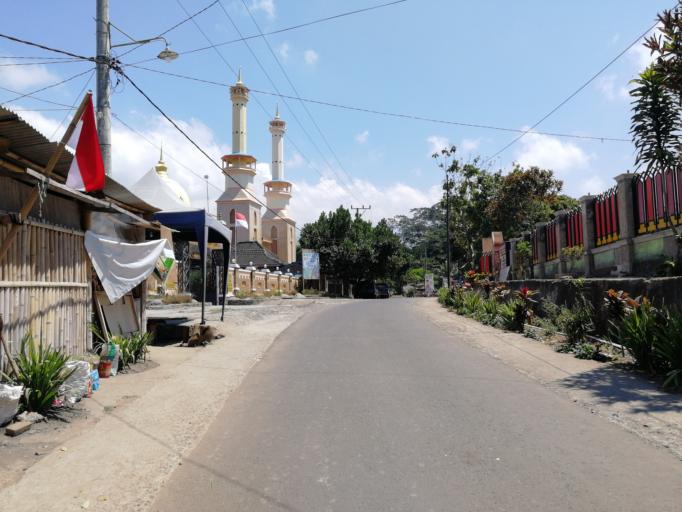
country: ID
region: West Nusa Tenggara
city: Tetebatu
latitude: -8.5537
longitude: 116.4200
